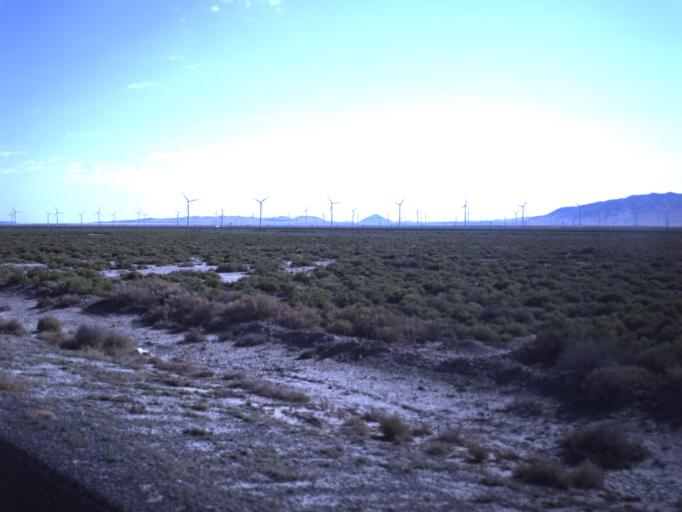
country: US
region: Utah
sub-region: Beaver County
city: Milford
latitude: 38.5336
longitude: -112.9912
